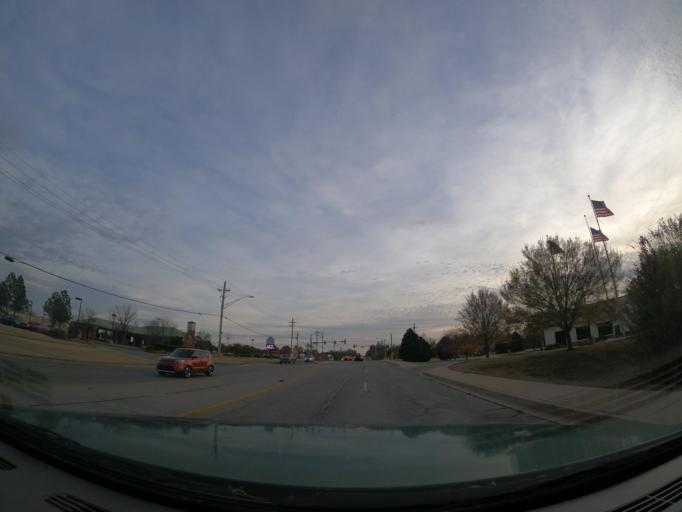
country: US
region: Oklahoma
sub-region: Tulsa County
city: Broken Arrow
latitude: 35.9896
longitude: -95.7976
